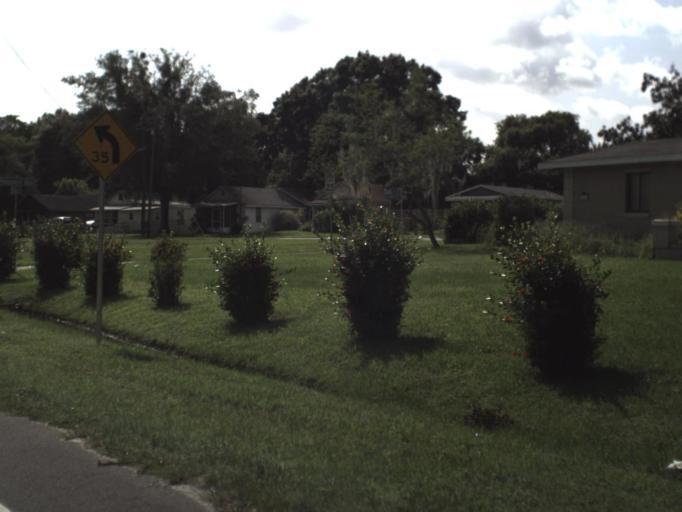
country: US
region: Florida
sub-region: Polk County
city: Eagle Lake
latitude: 27.9979
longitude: -81.7461
